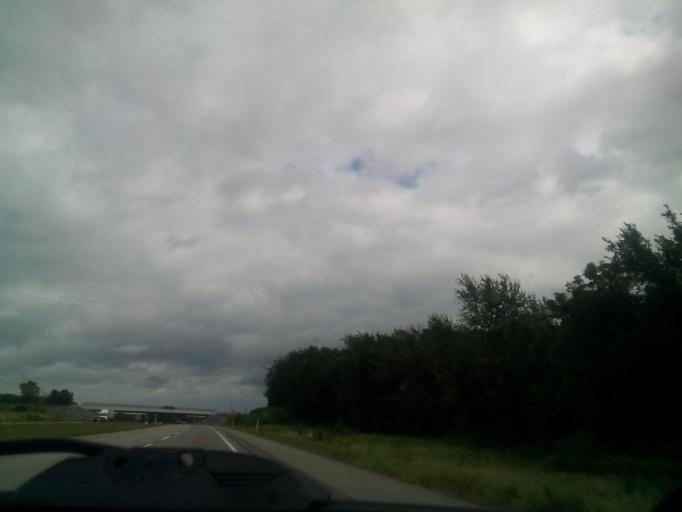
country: US
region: Indiana
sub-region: Steuben County
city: Fremont
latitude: 41.6960
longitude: -84.9109
